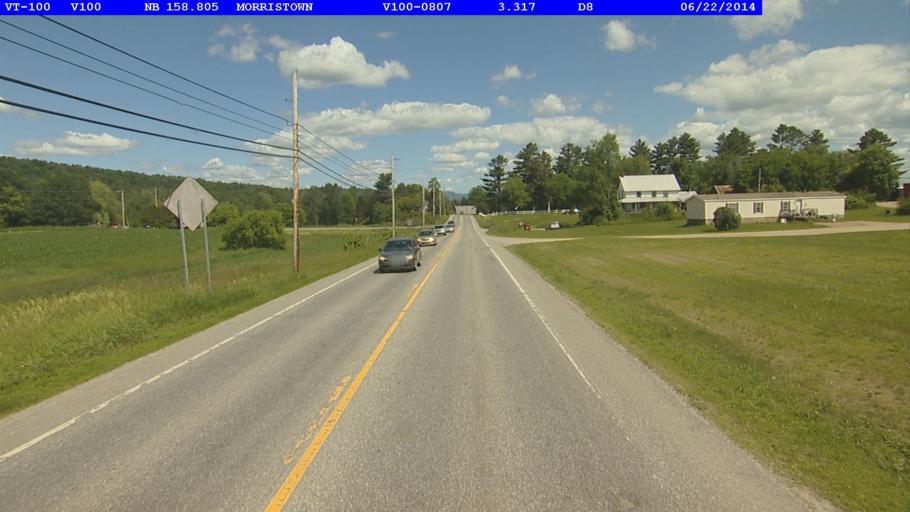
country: US
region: Vermont
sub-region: Lamoille County
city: Morristown
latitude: 44.5397
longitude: -72.6174
